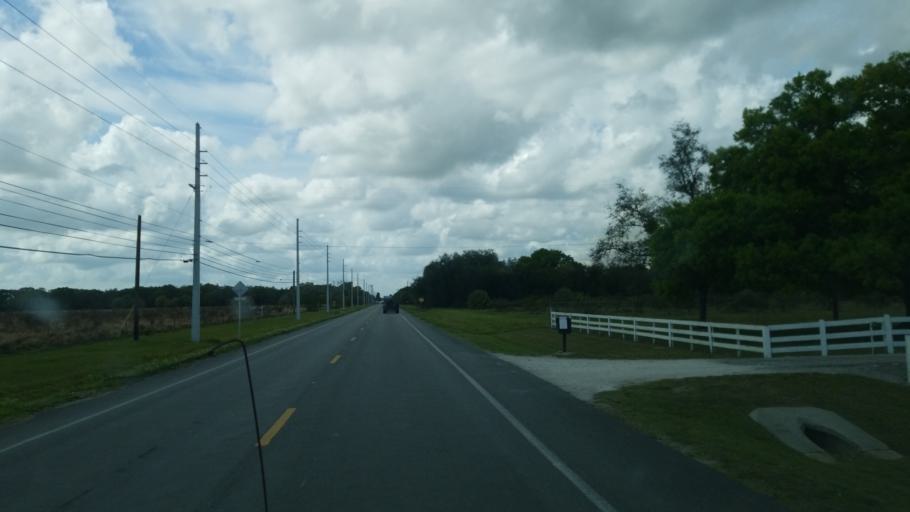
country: US
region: Florida
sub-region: Saint Lucie County
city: Lakewood Park
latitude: 27.4476
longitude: -80.4742
